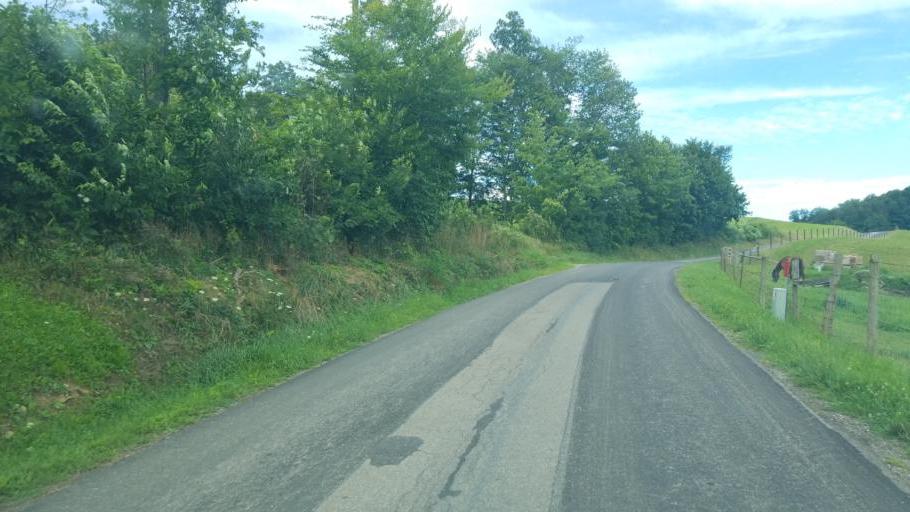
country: US
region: Ohio
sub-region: Holmes County
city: Millersburg
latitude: 40.4924
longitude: -81.8237
